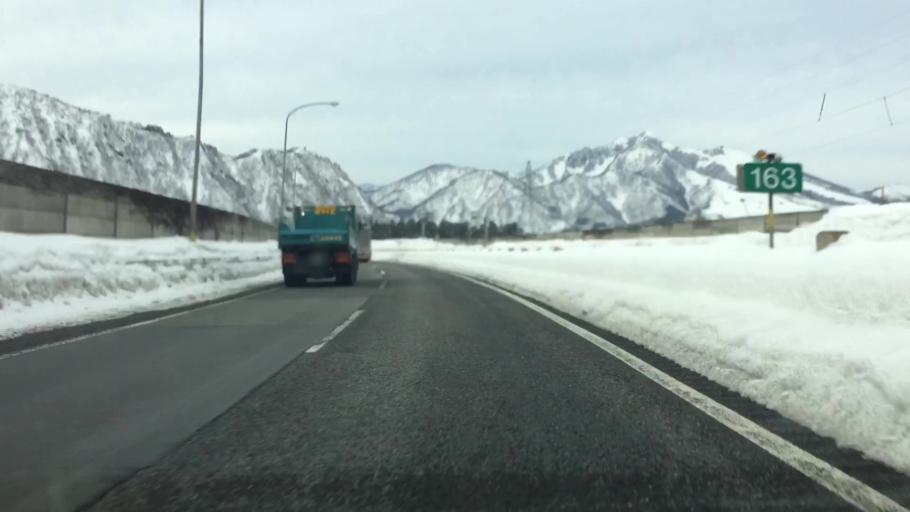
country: JP
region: Niigata
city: Shiozawa
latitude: 36.9046
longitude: 138.8470
